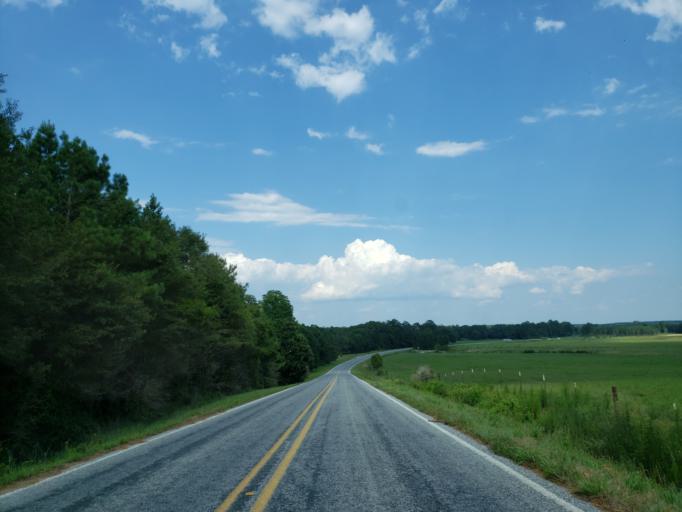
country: US
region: Mississippi
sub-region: Jones County
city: Ellisville
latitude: 31.6236
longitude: -89.3650
